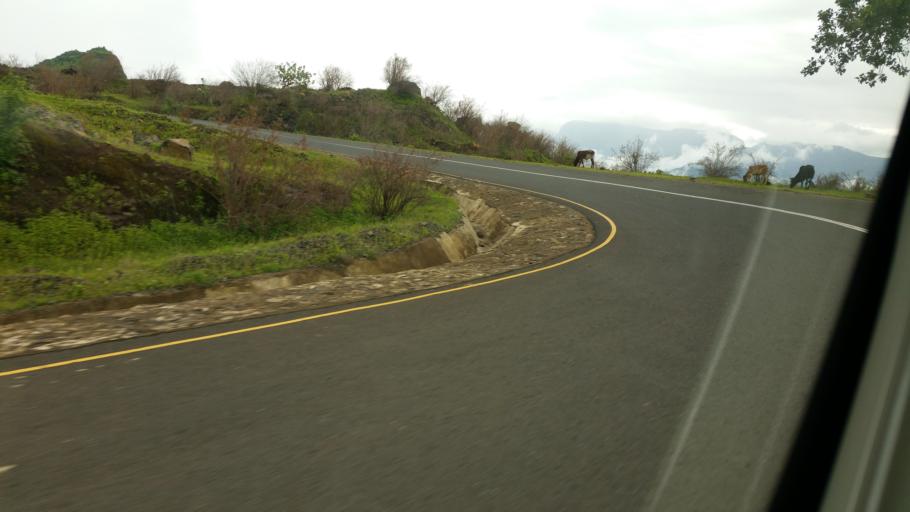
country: ET
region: Amhara
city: Debark'
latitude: 13.3525
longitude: 37.9250
